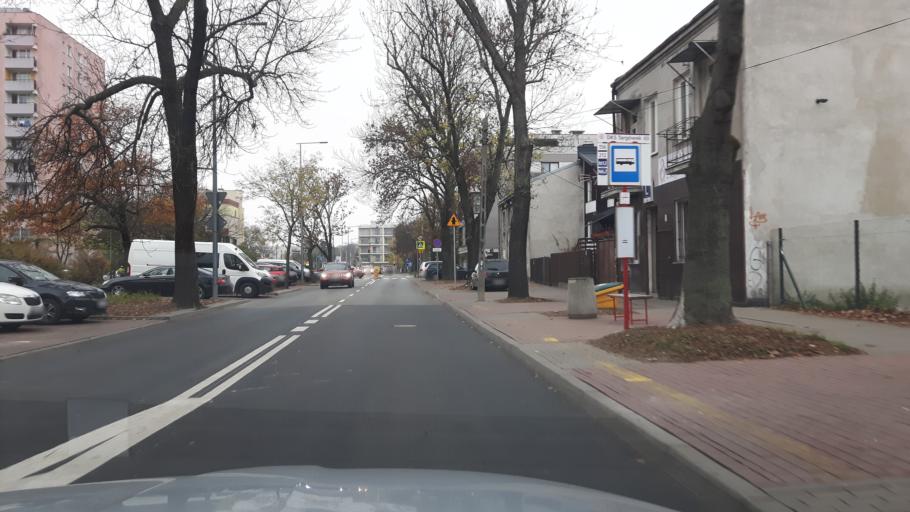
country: PL
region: Masovian Voivodeship
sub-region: Warszawa
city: Targowek
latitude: 52.2731
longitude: 21.0457
